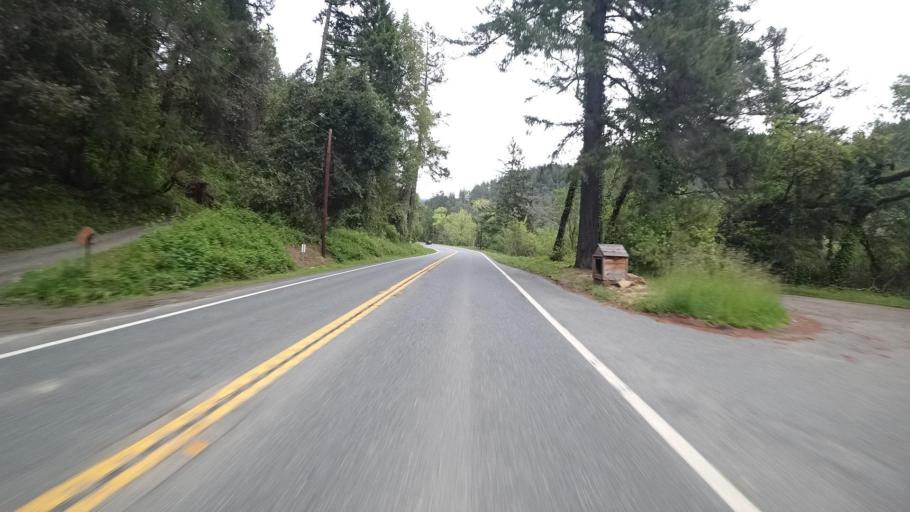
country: US
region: California
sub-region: Humboldt County
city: Willow Creek
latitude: 40.9861
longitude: -123.6382
